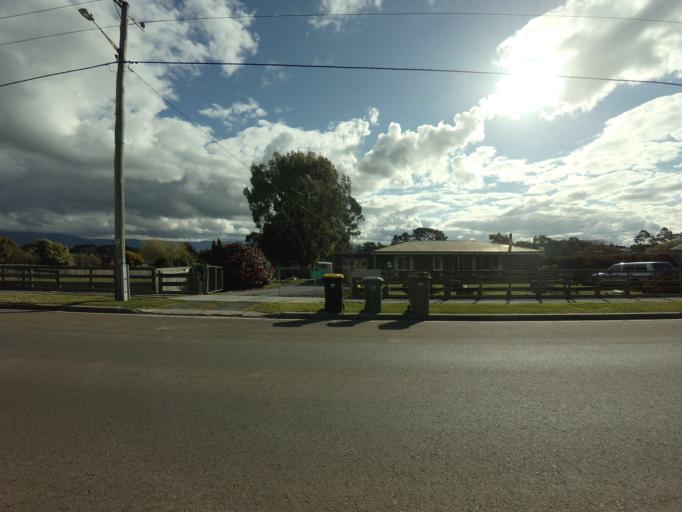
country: AU
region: Tasmania
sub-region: Northern Midlands
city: Longford
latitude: -41.6943
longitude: 147.0785
